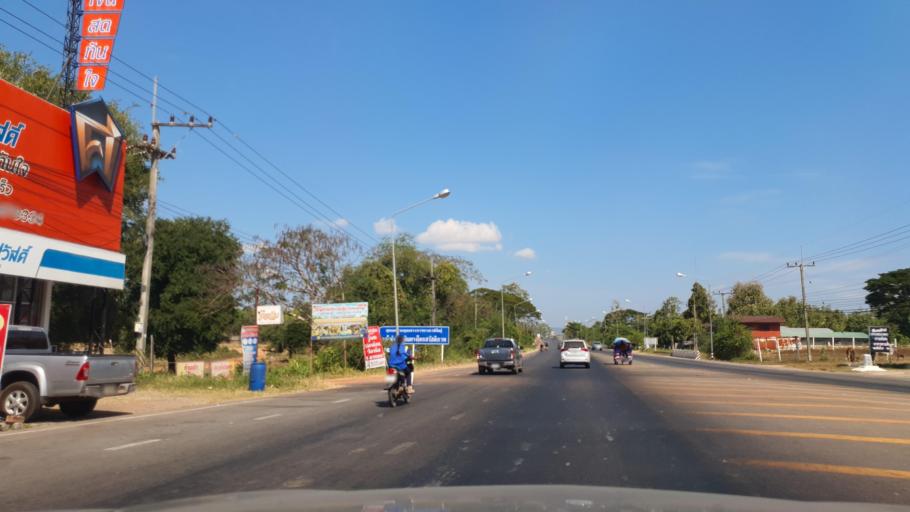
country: TH
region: Kalasin
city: Somdet
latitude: 16.7111
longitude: 103.7523
